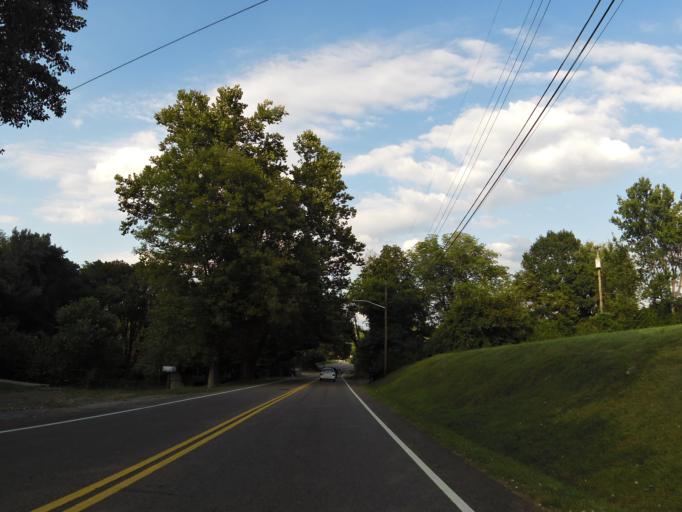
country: US
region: Tennessee
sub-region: Knox County
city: Knoxville
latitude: 35.9319
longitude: -83.9161
